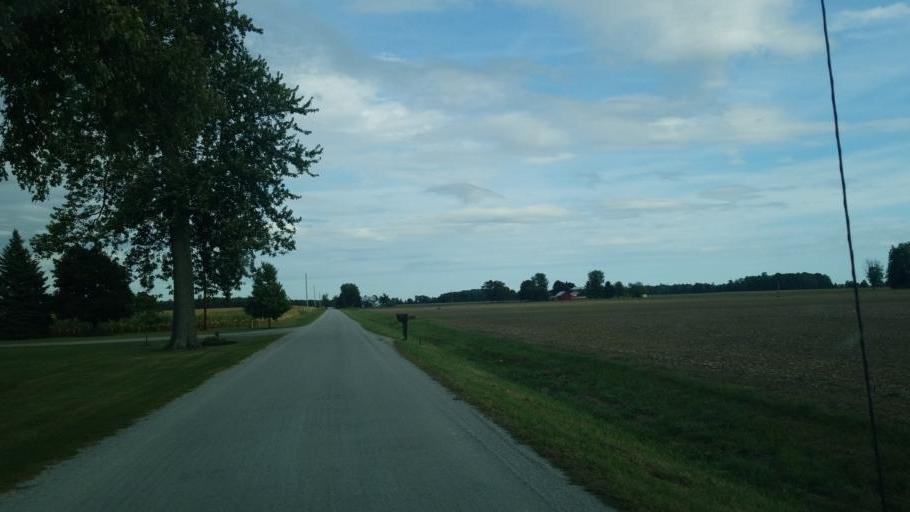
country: US
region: Ohio
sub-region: Hardin County
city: Forest
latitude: 40.8909
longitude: -83.4686
